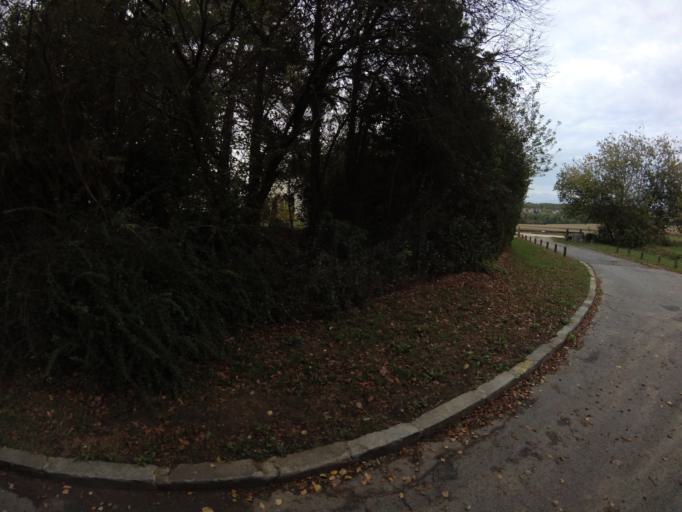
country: FR
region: Ile-de-France
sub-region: Departement de Seine-et-Marne
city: Collegien
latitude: 48.8440
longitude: 2.6774
